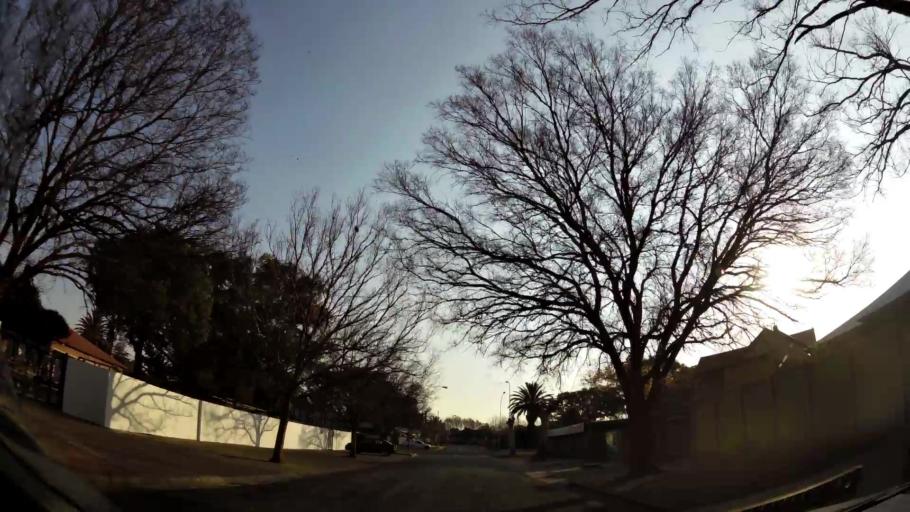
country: ZA
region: Gauteng
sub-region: Ekurhuleni Metropolitan Municipality
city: Springs
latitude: -26.2916
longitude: 28.4460
